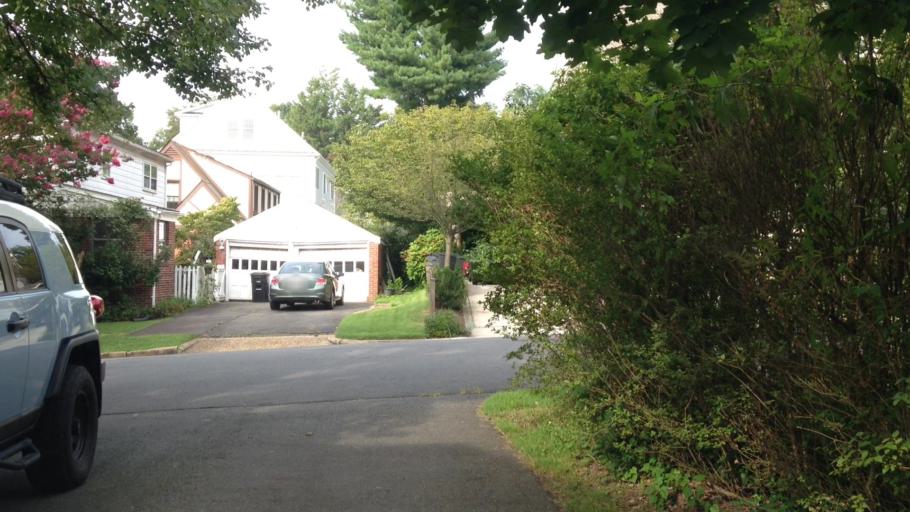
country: US
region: Virginia
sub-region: Fairfax County
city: Seven Corners
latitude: 38.8992
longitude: -77.1385
